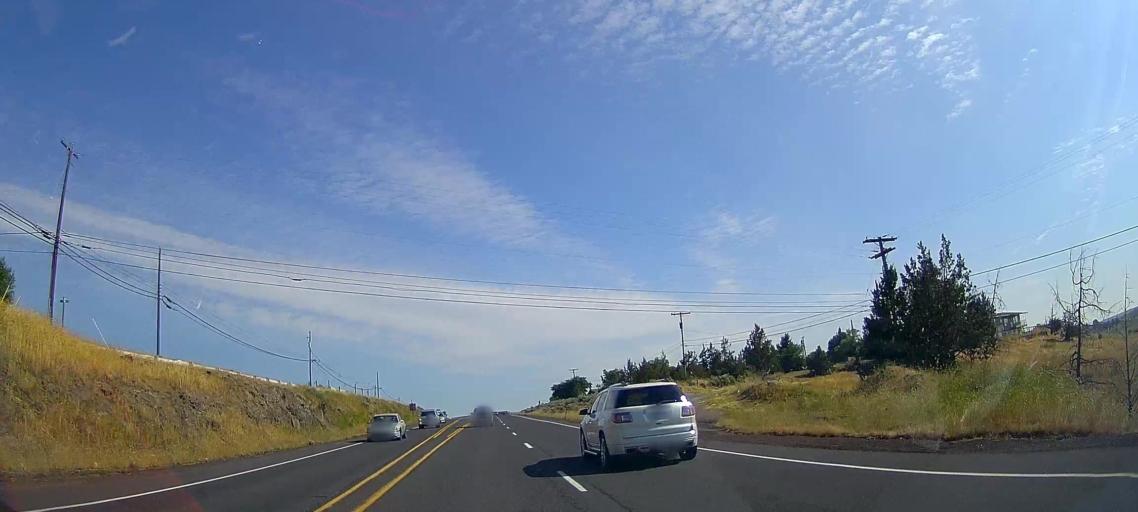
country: US
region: Oregon
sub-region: Jefferson County
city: Madras
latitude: 44.6500
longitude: -121.1290
